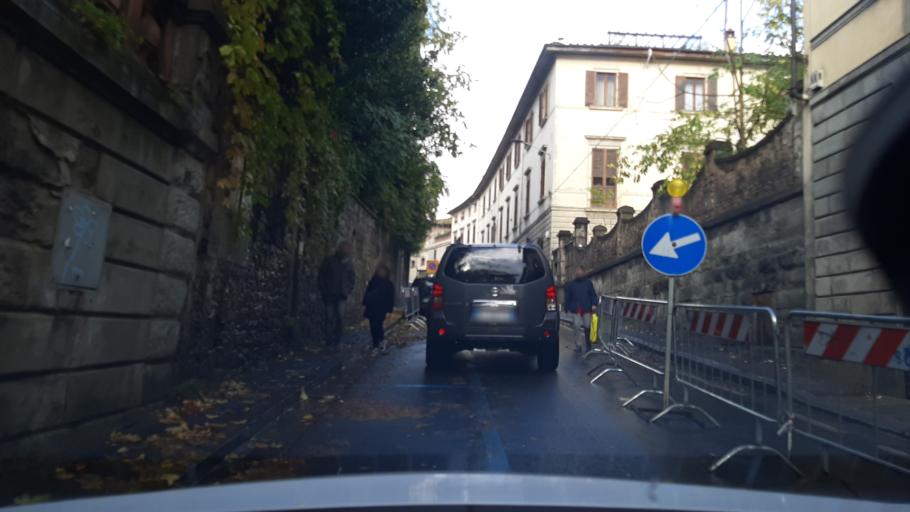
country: IT
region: Tuscany
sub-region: Province of Florence
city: Florence
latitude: 43.7889
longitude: 11.2627
